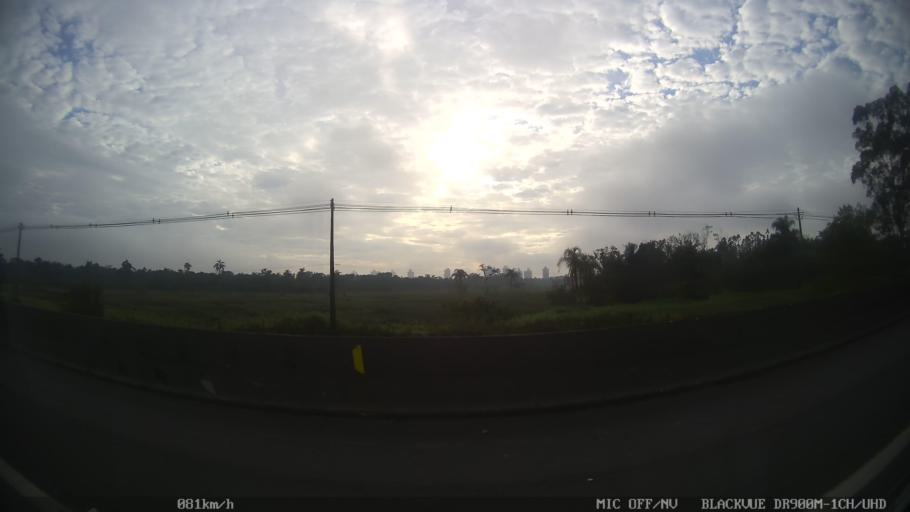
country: BR
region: Santa Catarina
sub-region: Penha
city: Penha
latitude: -26.7507
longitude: -48.6927
